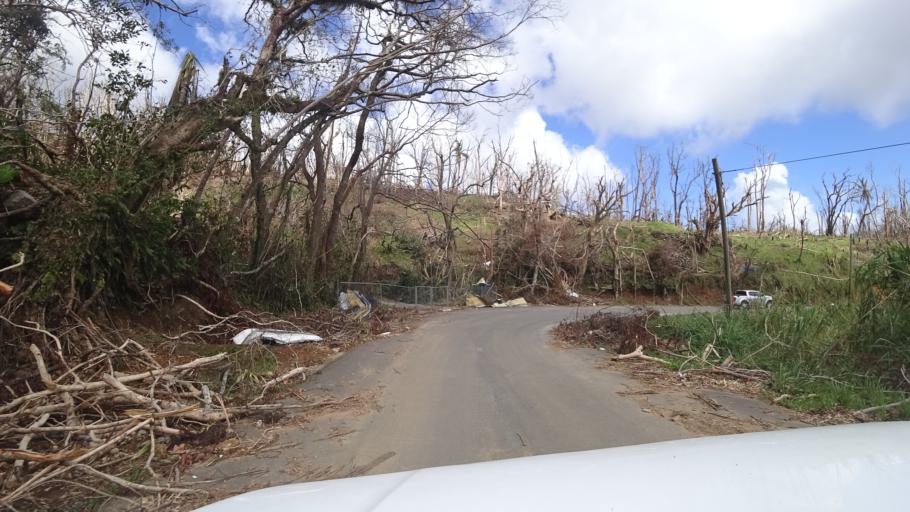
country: DM
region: Saint Luke
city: Pointe Michel
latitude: 15.2689
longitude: -61.3430
